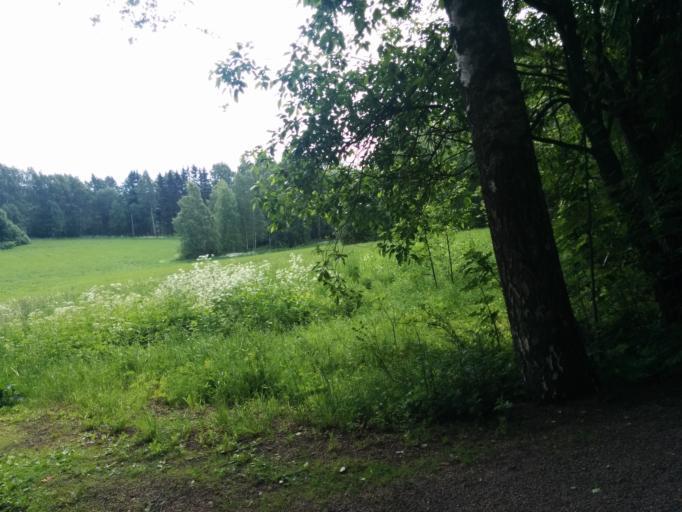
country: FI
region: Uusimaa
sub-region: Helsinki
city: Vantaa
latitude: 60.2379
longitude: 25.1296
